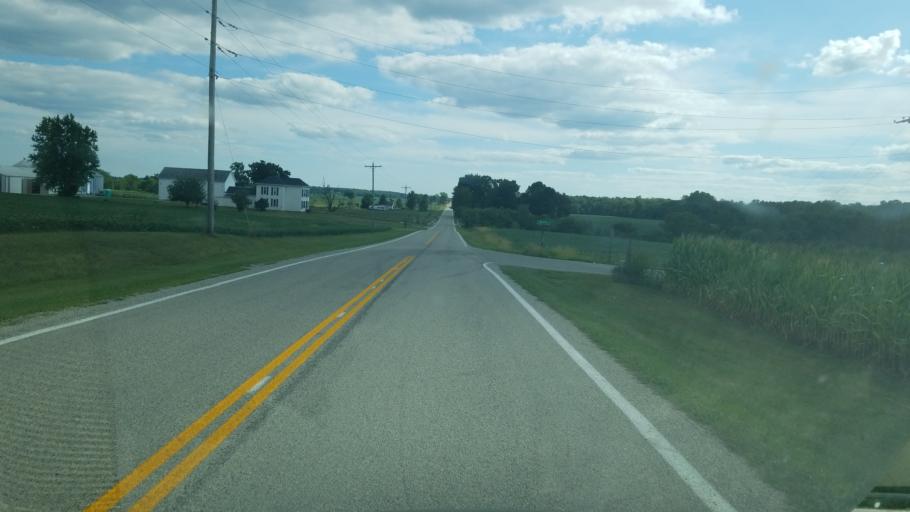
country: US
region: Ohio
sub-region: Logan County
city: De Graff
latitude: 40.2402
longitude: -83.9389
